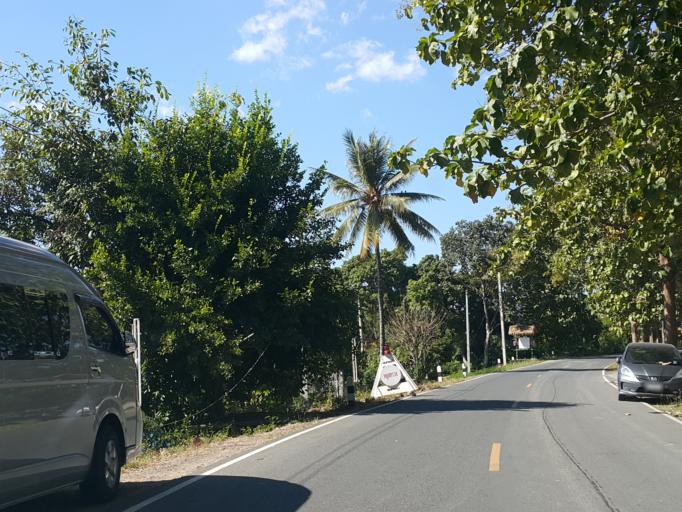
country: TH
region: Chiang Mai
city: San Sai
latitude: 18.8979
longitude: 99.1382
